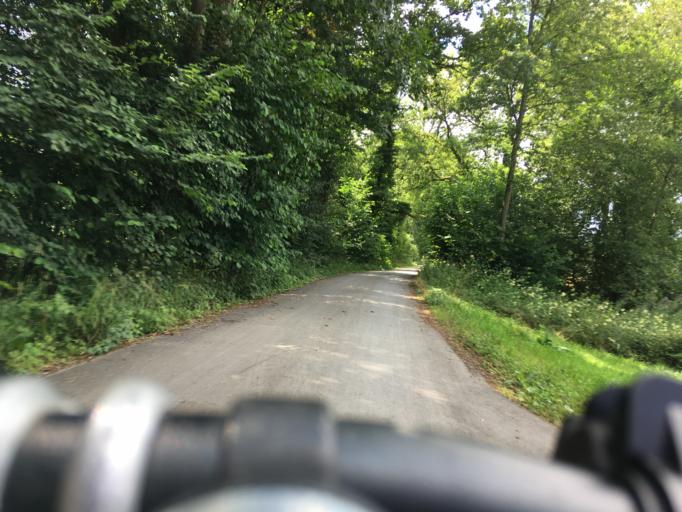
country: DE
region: Baden-Wuerttemberg
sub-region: Freiburg Region
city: Busingen
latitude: 47.6870
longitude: 8.6930
